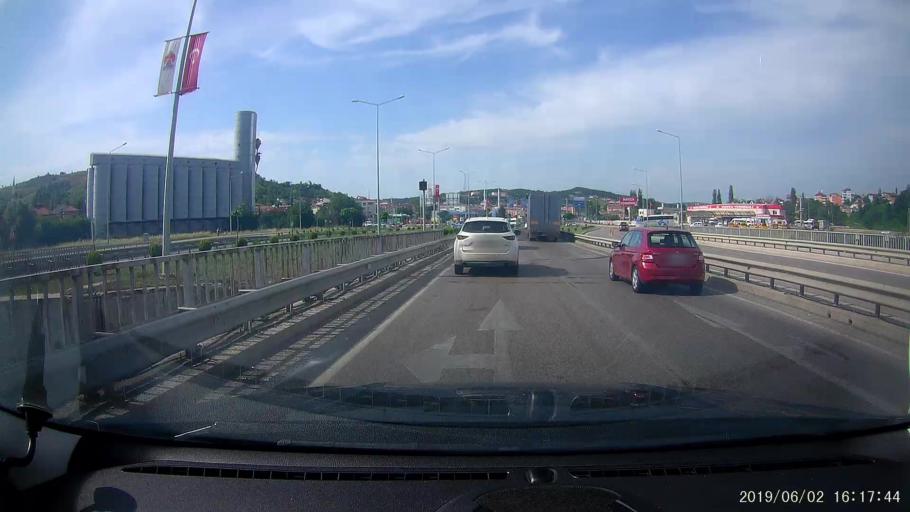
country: TR
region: Samsun
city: Havza
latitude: 40.9601
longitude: 35.6661
